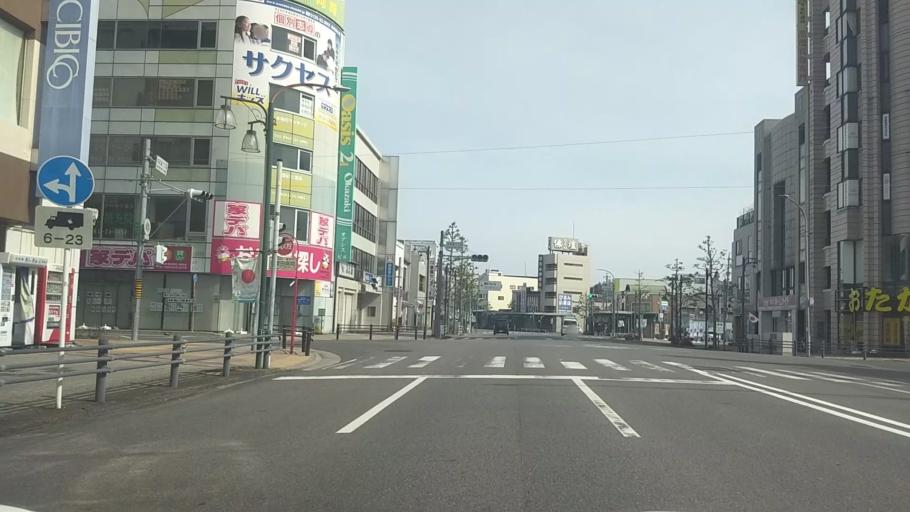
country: JP
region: Aichi
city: Okazaki
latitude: 34.9591
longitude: 137.1639
